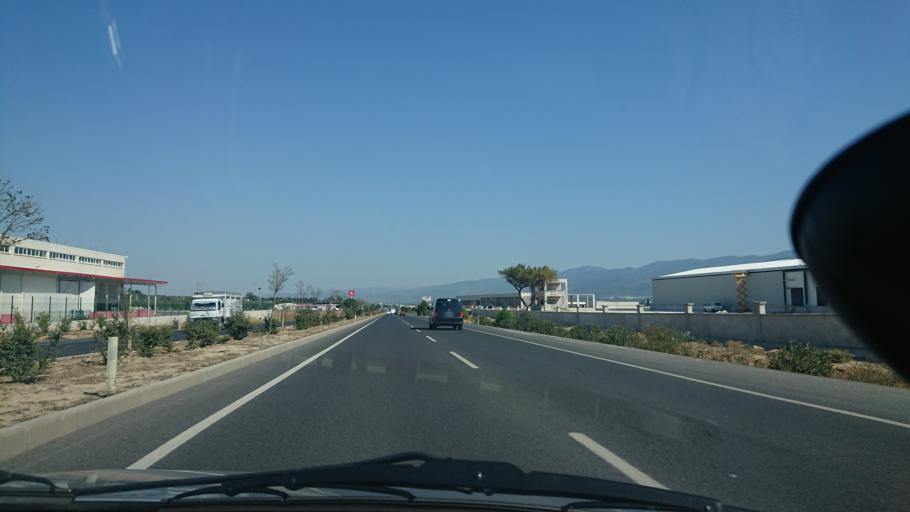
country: TR
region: Izmir
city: Kemalpasa
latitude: 38.4497
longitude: 27.4957
